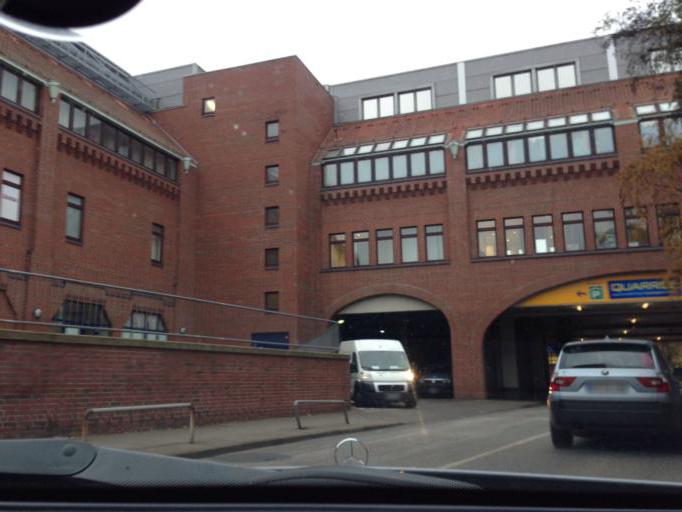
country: DE
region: Hamburg
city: Marienthal
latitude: 53.5737
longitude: 10.0680
